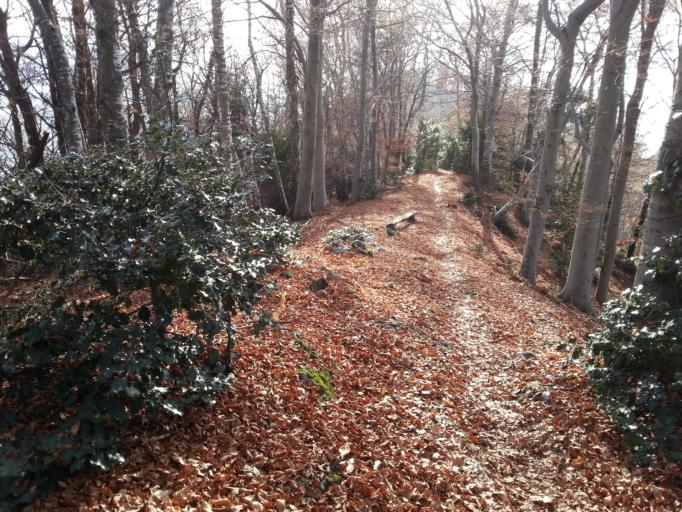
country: IT
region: Lombardy
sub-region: Provincia di Como
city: Maslianico
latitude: 45.8571
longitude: 9.0506
